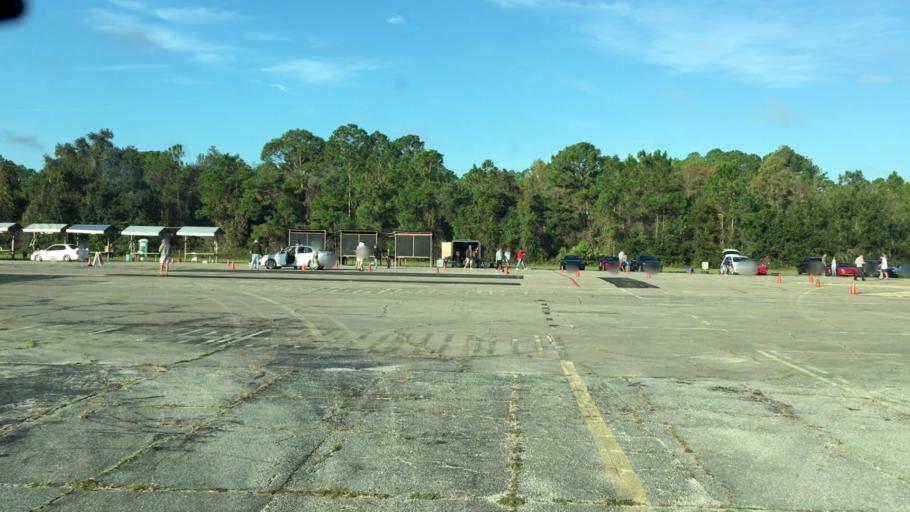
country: US
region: Florida
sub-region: Volusia County
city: North DeLand
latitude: 29.0765
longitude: -81.2864
